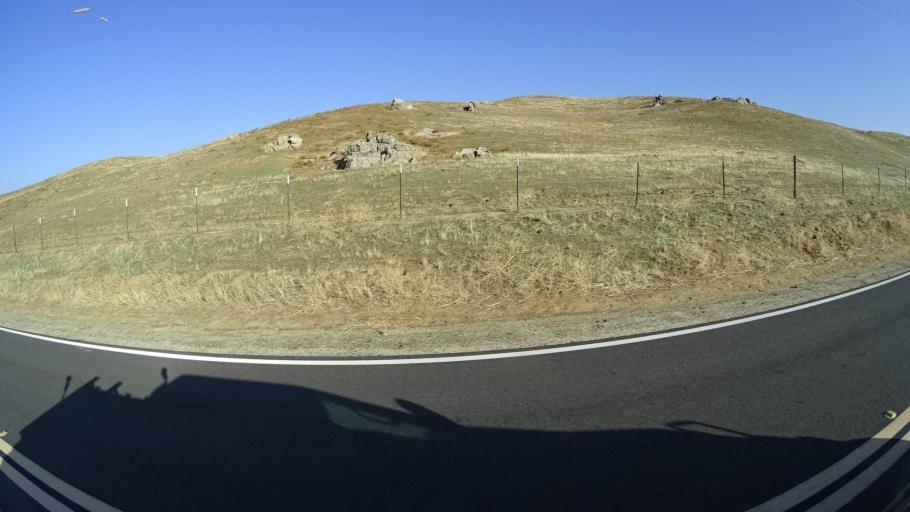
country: US
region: California
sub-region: Tulare County
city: Richgrove
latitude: 35.7419
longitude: -118.8908
